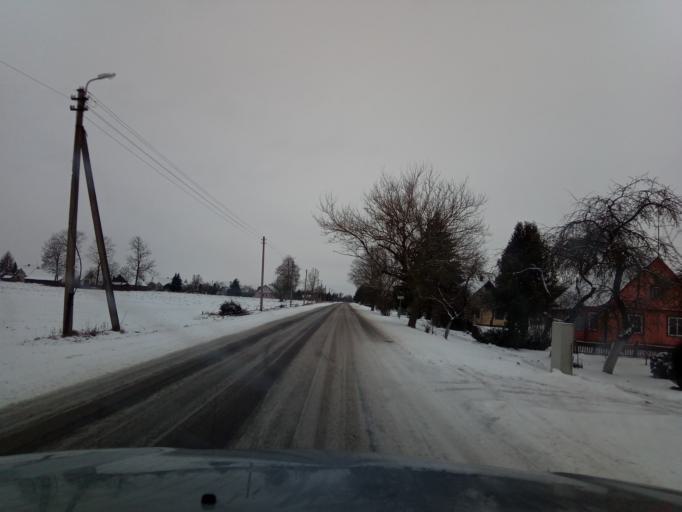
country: LT
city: Ramygala
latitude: 55.4930
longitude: 24.4915
